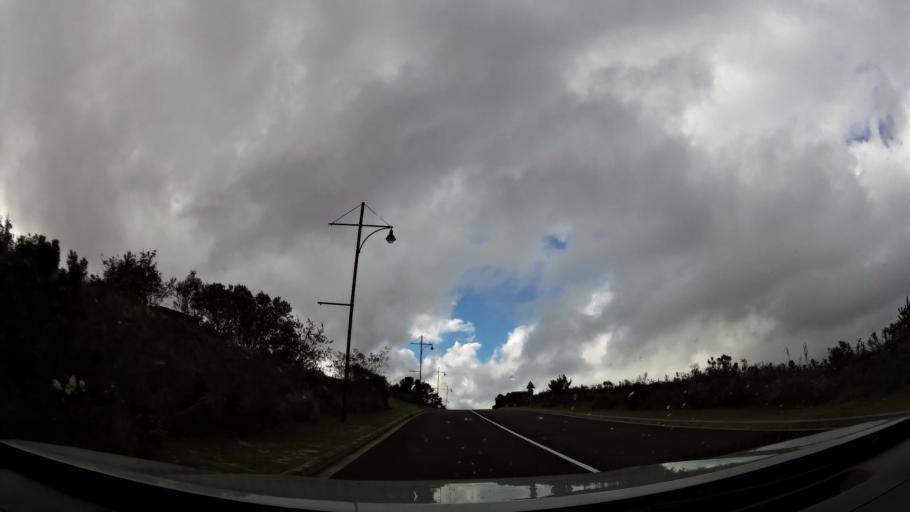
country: ZA
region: Western Cape
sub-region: Eden District Municipality
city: Knysna
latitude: -34.0666
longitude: 23.0997
